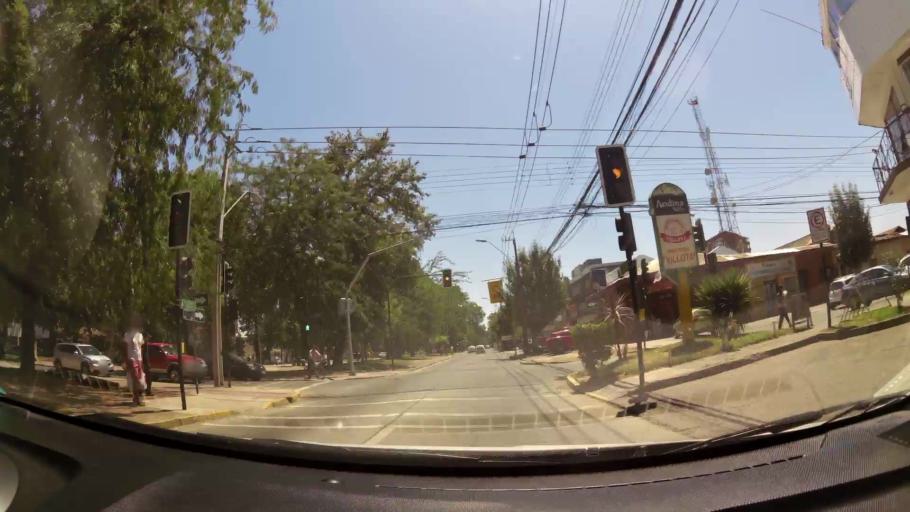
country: CL
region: Maule
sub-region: Provincia de Curico
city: Curico
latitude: -34.9878
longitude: -71.2335
